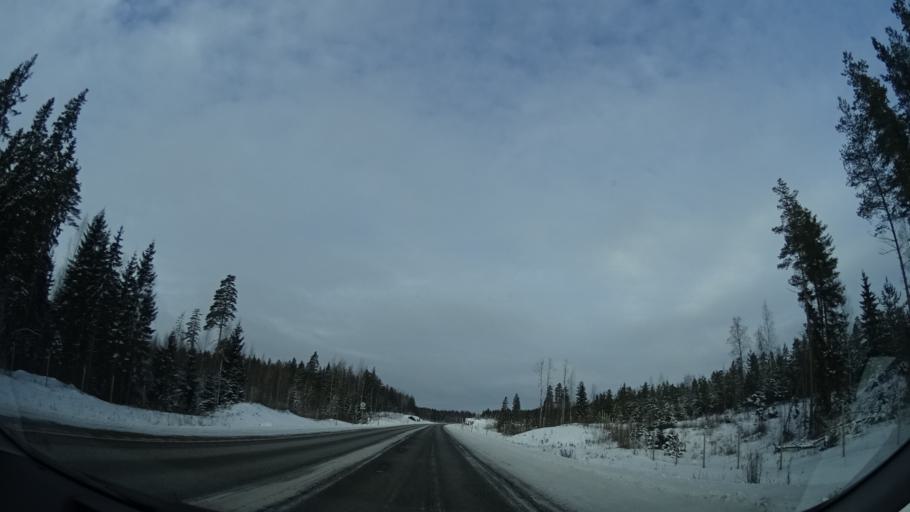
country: FI
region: Uusimaa
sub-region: Helsinki
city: Karkkila
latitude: 60.5920
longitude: 24.1049
